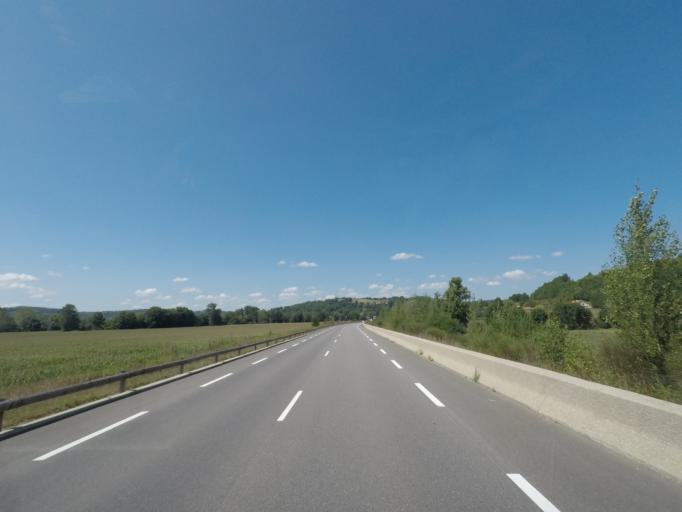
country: FR
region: Midi-Pyrenees
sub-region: Departement du Lot
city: Figeac
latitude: 44.5932
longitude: 1.9832
